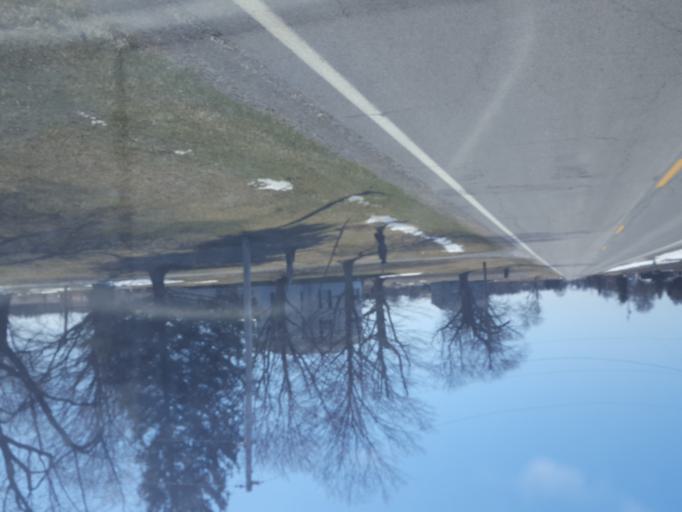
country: US
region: Ohio
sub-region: Wyandot County
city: Upper Sandusky
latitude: 40.7380
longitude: -83.2686
